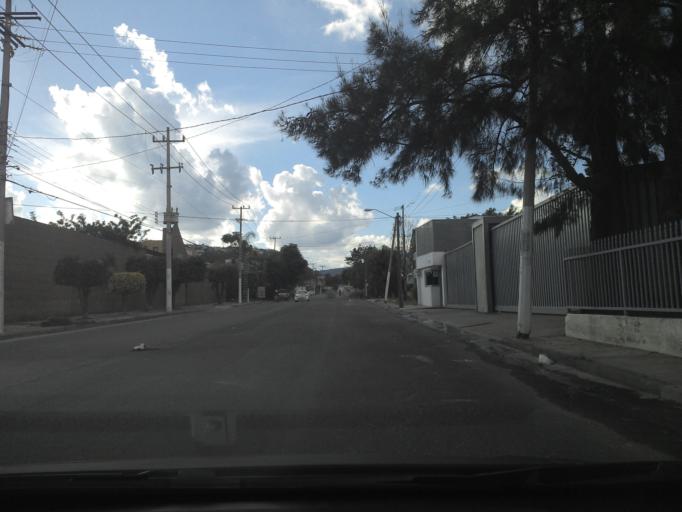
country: MX
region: Jalisco
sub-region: Tlajomulco de Zuniga
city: Palomar
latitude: 20.6174
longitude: -103.4495
